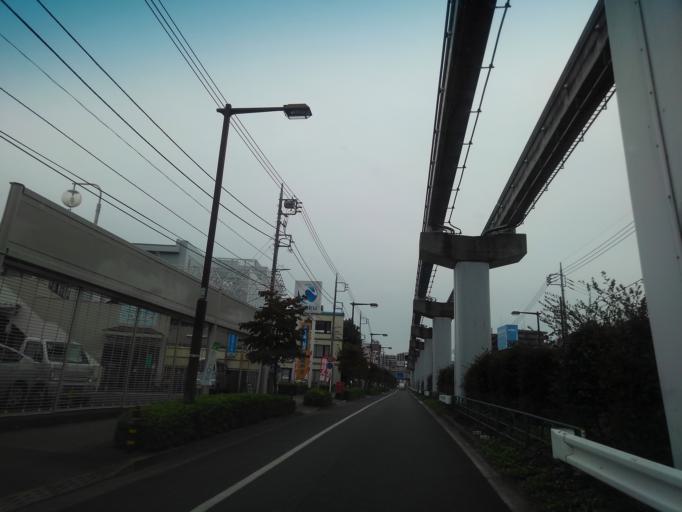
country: JP
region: Tokyo
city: Higashimurayama-shi
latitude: 35.7419
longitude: 139.4161
